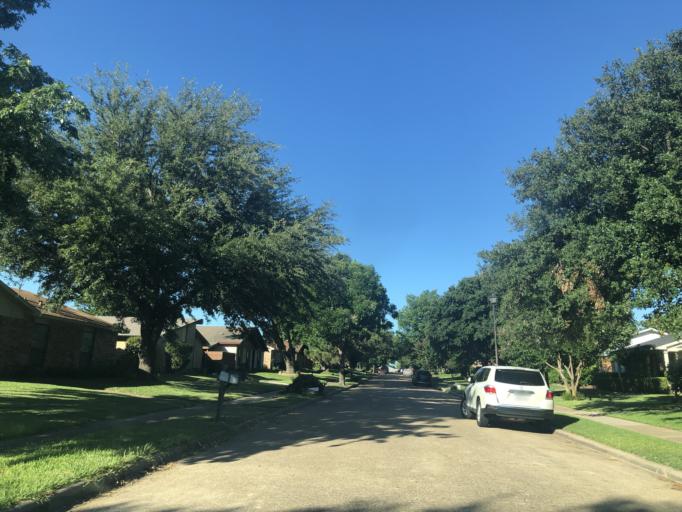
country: US
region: Texas
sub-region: Dallas County
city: Duncanville
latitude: 32.6413
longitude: -96.9503
